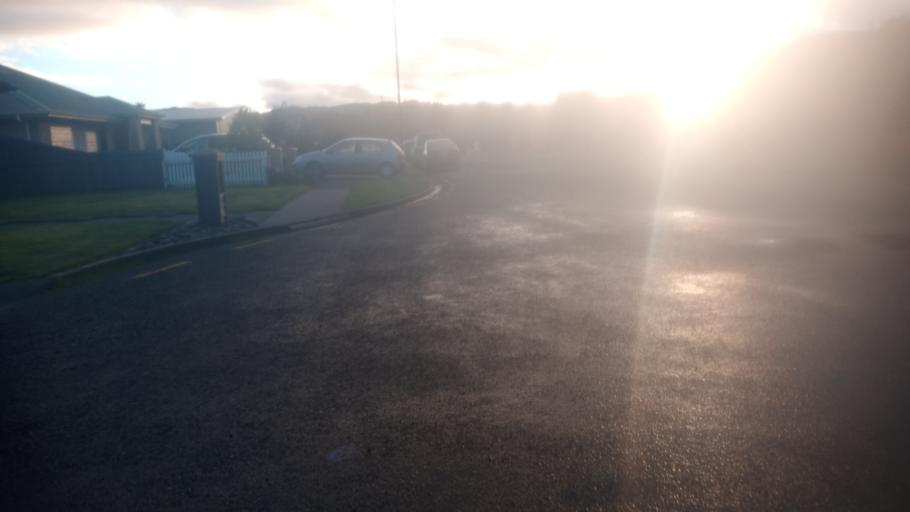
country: NZ
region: Gisborne
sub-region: Gisborne District
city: Gisborne
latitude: -38.6400
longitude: 177.9901
